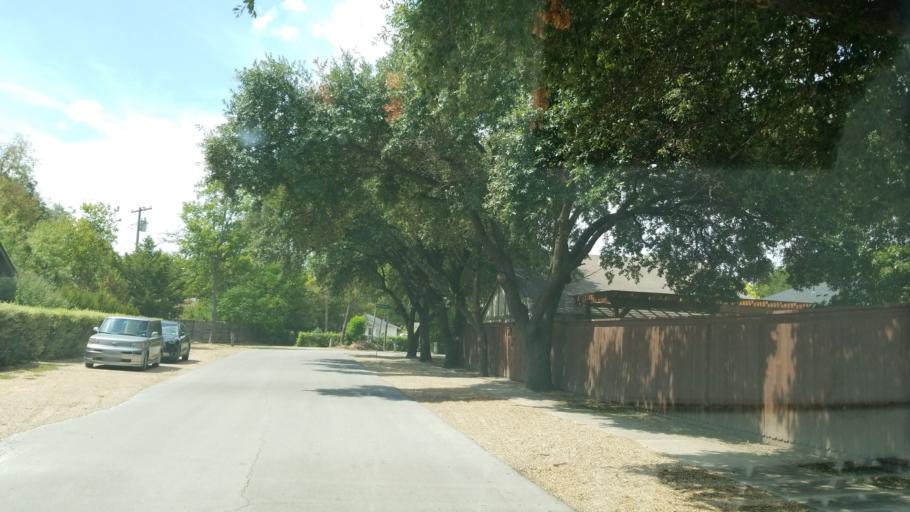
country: US
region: Texas
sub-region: Dallas County
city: Dallas
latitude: 32.7539
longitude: -96.8434
